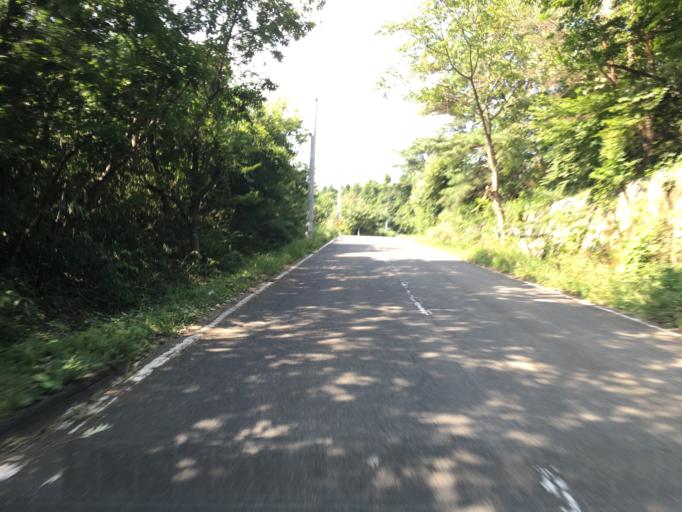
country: JP
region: Fukushima
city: Nihommatsu
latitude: 37.5705
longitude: 140.3847
